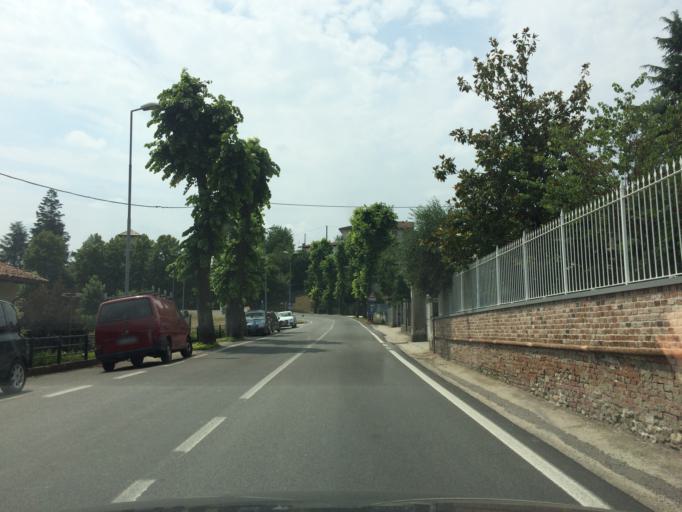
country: IT
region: Piedmont
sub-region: Provincia di Cuneo
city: Barolo
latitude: 44.6098
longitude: 7.9403
